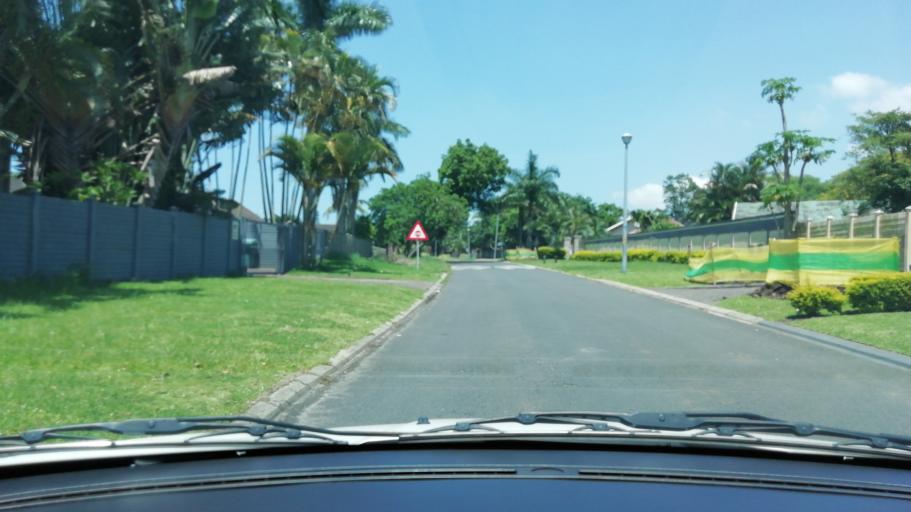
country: ZA
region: KwaZulu-Natal
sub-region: uThungulu District Municipality
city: Richards Bay
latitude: -28.7365
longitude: 32.0548
